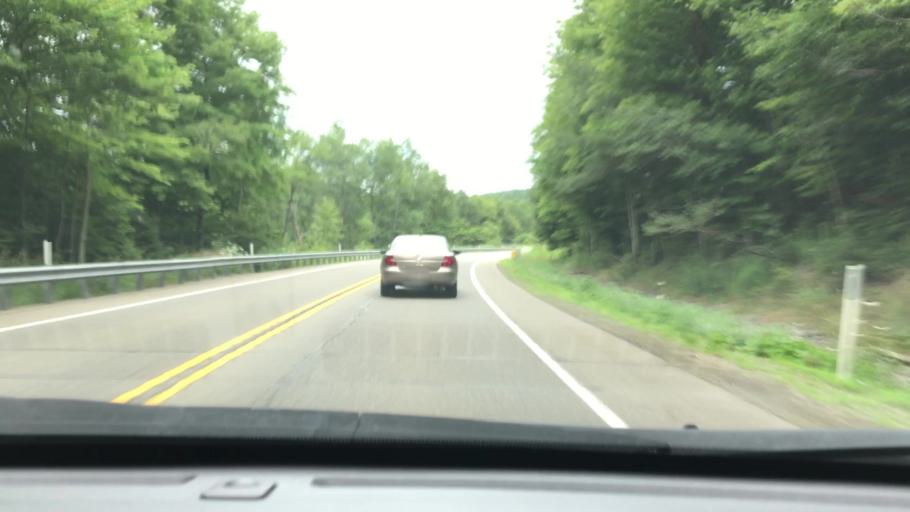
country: US
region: Pennsylvania
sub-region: Elk County
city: Johnsonburg
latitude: 41.5187
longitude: -78.6796
